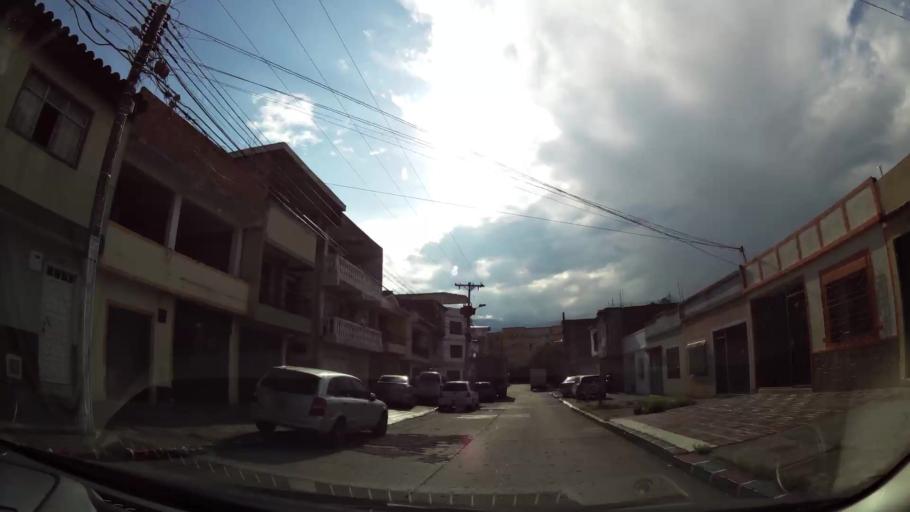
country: CO
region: Valle del Cauca
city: Cali
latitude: 3.4268
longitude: -76.5251
